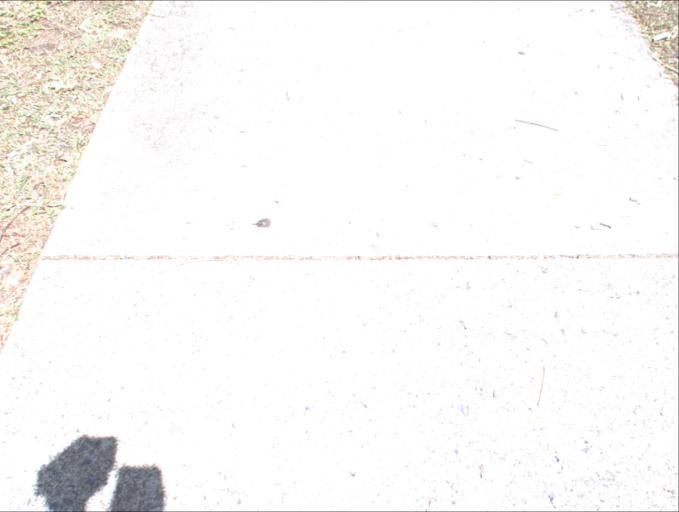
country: AU
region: Queensland
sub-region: Logan
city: Woodridge
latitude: -27.6341
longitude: 153.1057
